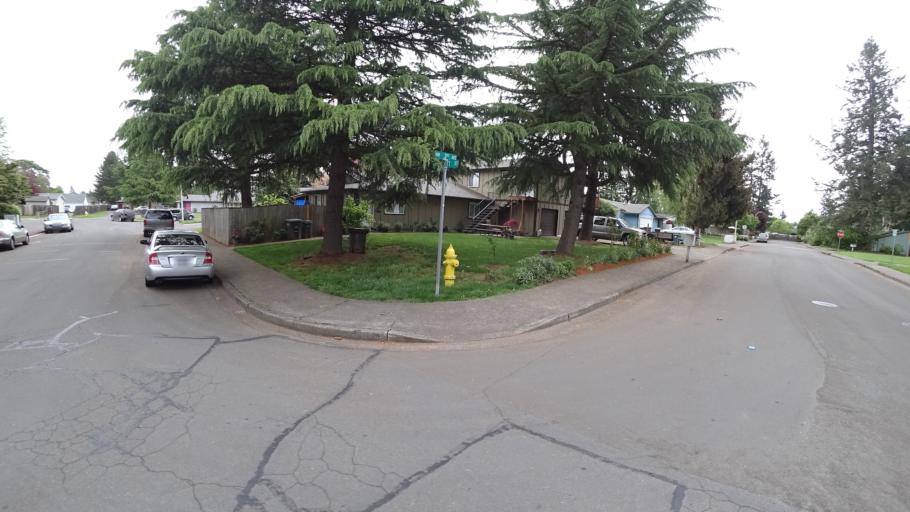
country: US
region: Oregon
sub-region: Washington County
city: Hillsboro
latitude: 45.5423
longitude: -122.9983
